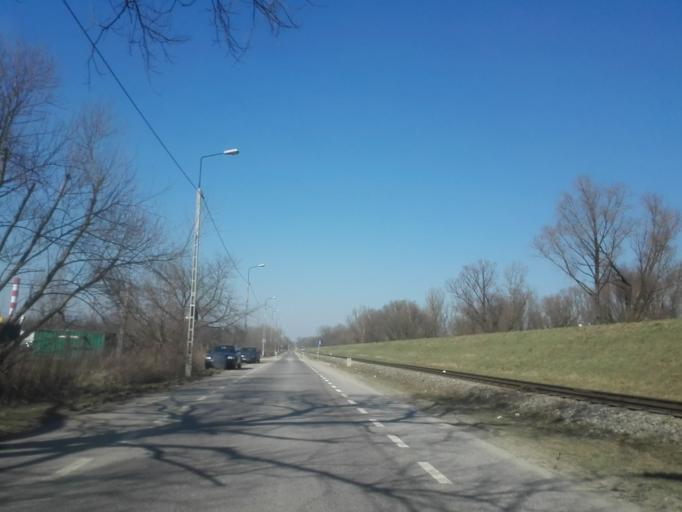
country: PL
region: Masovian Voivodeship
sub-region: Warszawa
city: Wilanow
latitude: 52.1768
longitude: 21.1166
